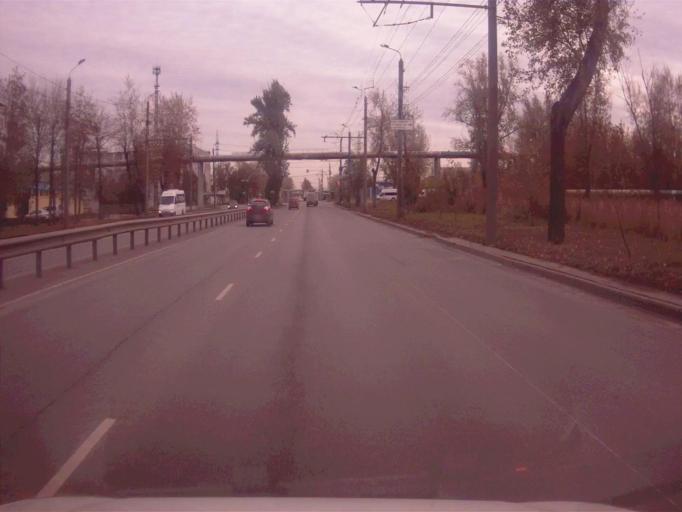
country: RU
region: Chelyabinsk
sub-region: Gorod Chelyabinsk
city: Chelyabinsk
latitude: 55.1348
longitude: 61.4660
